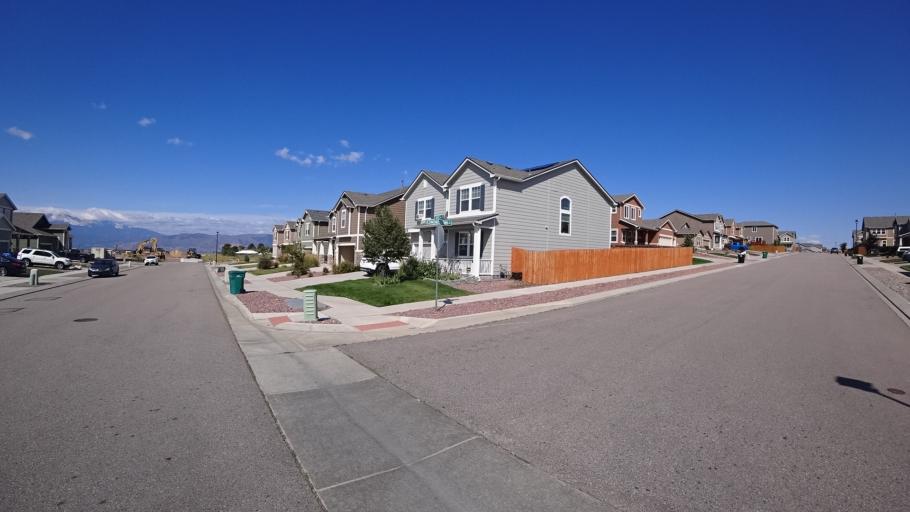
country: US
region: Colorado
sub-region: El Paso County
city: Cimarron Hills
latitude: 38.9279
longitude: -104.7099
